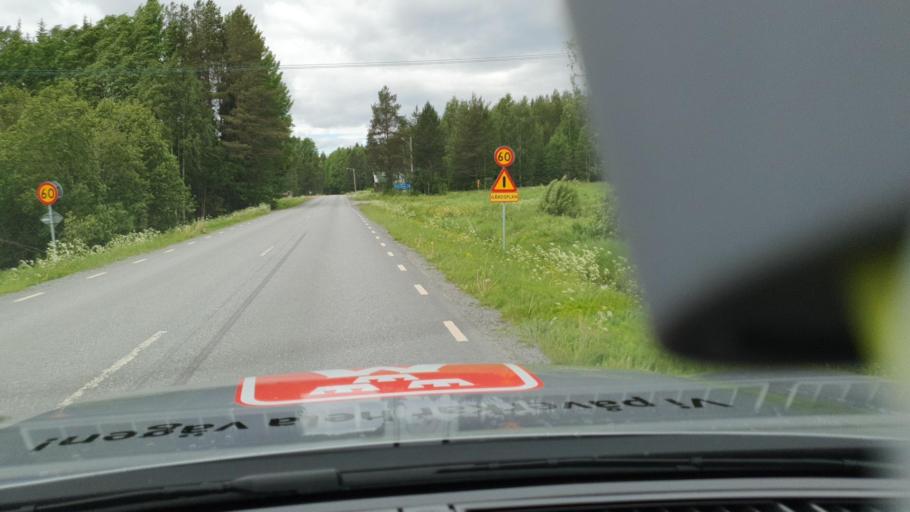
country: SE
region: Norrbotten
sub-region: Lulea Kommun
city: Sodra Sunderbyn
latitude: 65.8283
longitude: 21.9706
